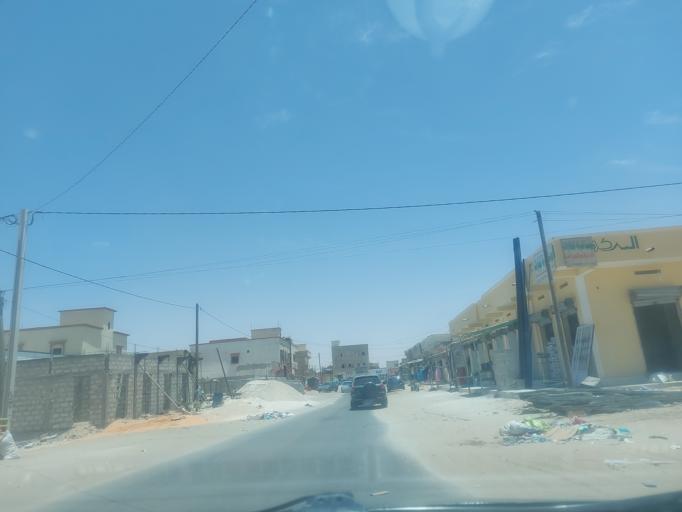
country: MR
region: Nouakchott
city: Nouakchott
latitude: 18.0682
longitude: -15.9447
